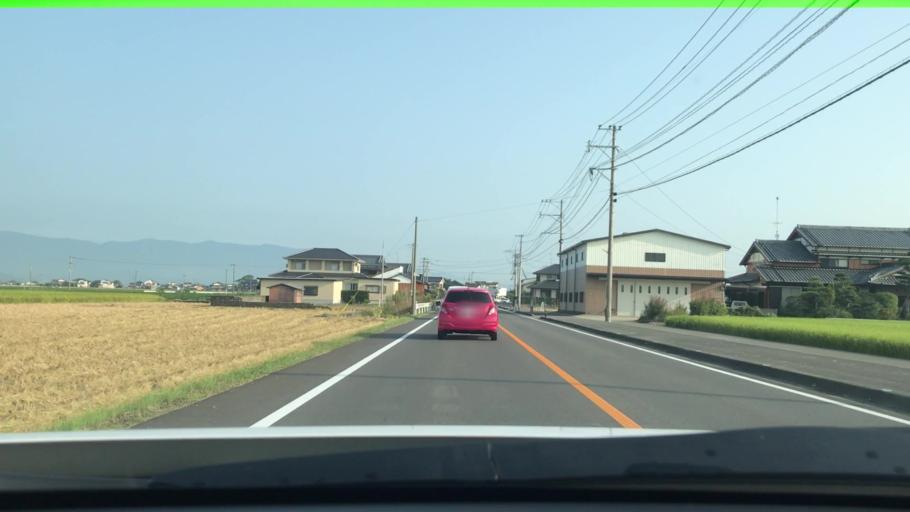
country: JP
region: Saga Prefecture
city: Saga-shi
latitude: 33.2063
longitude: 130.2061
